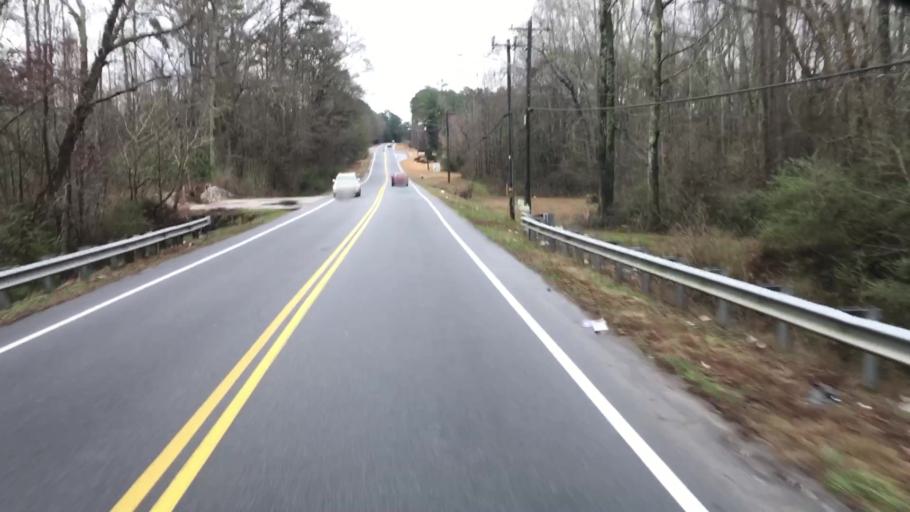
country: US
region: Georgia
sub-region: Gwinnett County
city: Snellville
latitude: 33.8266
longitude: -83.9856
